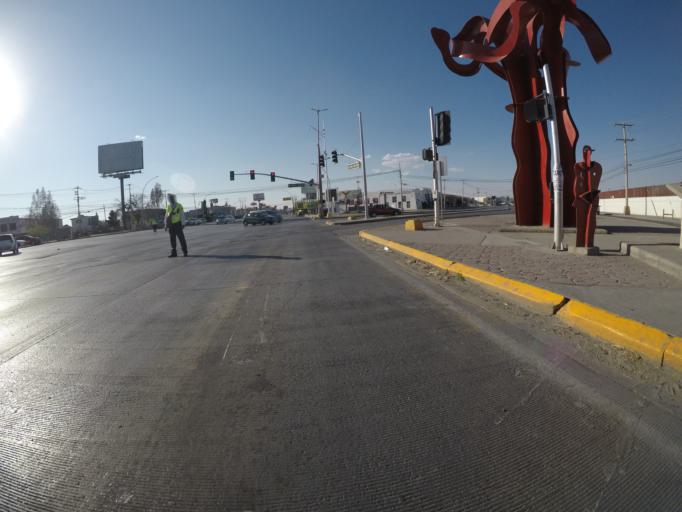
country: MX
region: Chihuahua
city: Ciudad Juarez
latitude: 31.7036
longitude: -106.4017
